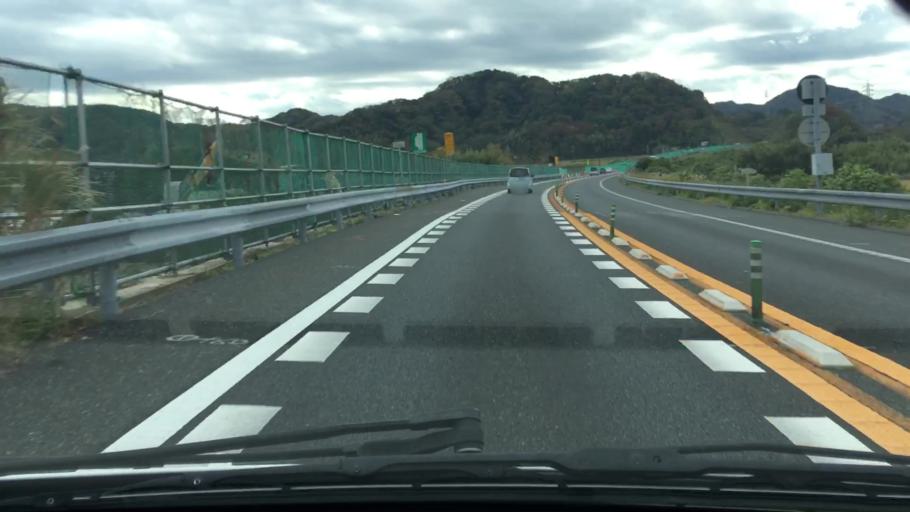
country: JP
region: Chiba
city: Kimitsu
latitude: 35.2174
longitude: 139.8859
